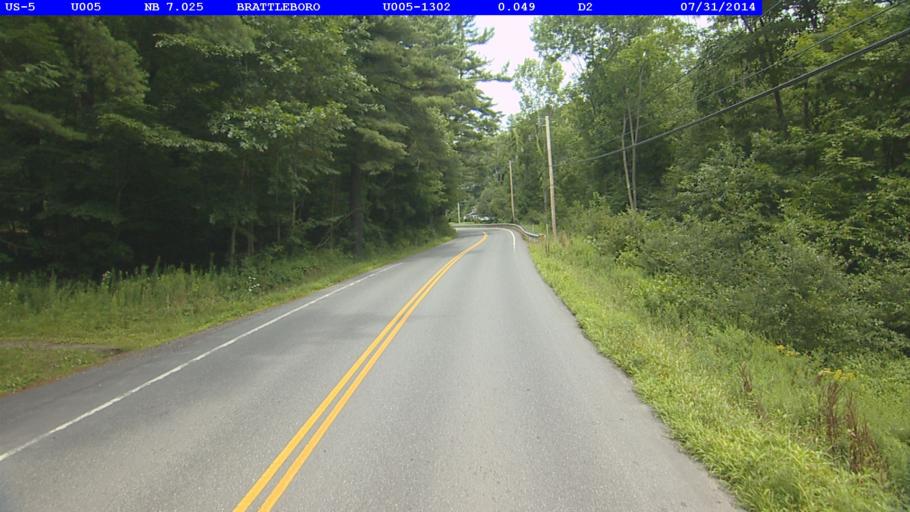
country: US
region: Vermont
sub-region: Windham County
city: Brattleboro
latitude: 42.8252
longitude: -72.5745
